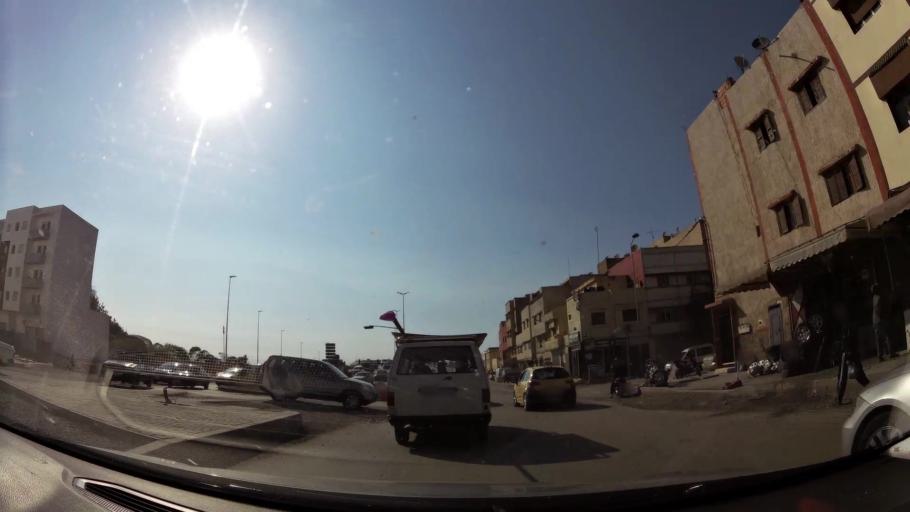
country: MA
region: Rabat-Sale-Zemmour-Zaer
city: Sale
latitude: 34.0573
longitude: -6.7981
